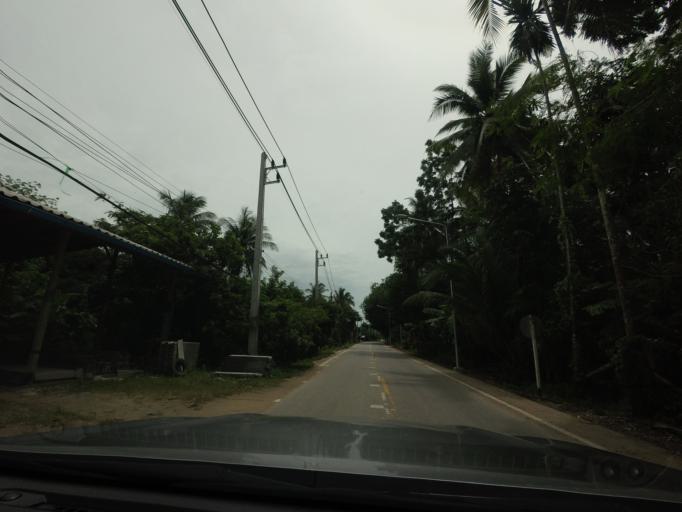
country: TH
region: Pattani
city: Kapho
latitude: 6.5743
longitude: 101.5350
